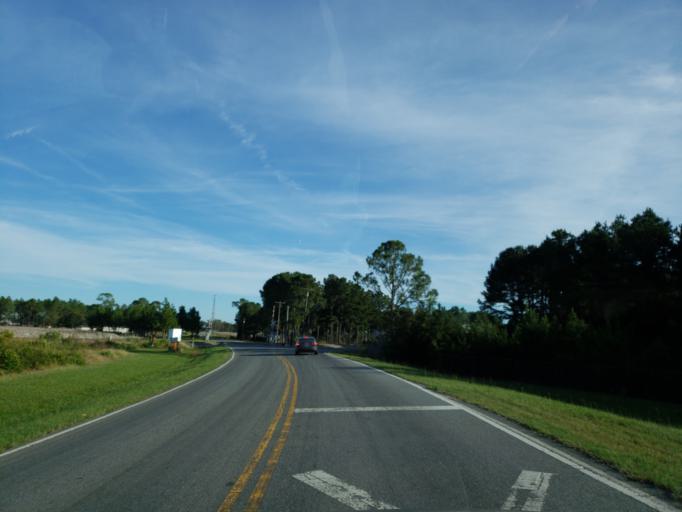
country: US
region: Georgia
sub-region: Dooly County
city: Vienna
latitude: 32.0778
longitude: -83.7878
